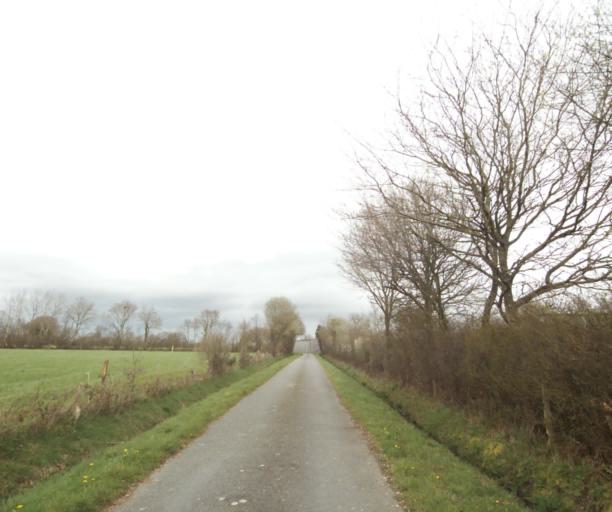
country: FR
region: Pays de la Loire
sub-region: Departement de la Loire-Atlantique
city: Bouvron
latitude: 47.4388
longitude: -1.8568
